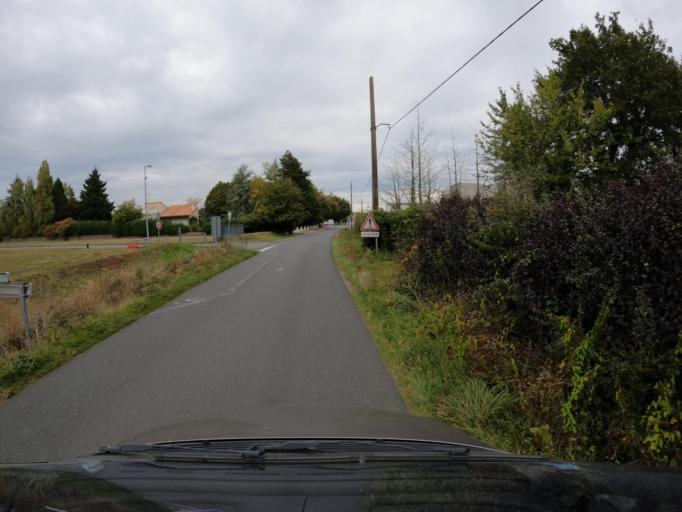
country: FR
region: Pays de la Loire
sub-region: Departement de Maine-et-Loire
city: La Seguiniere
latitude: 47.0539
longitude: -0.9402
